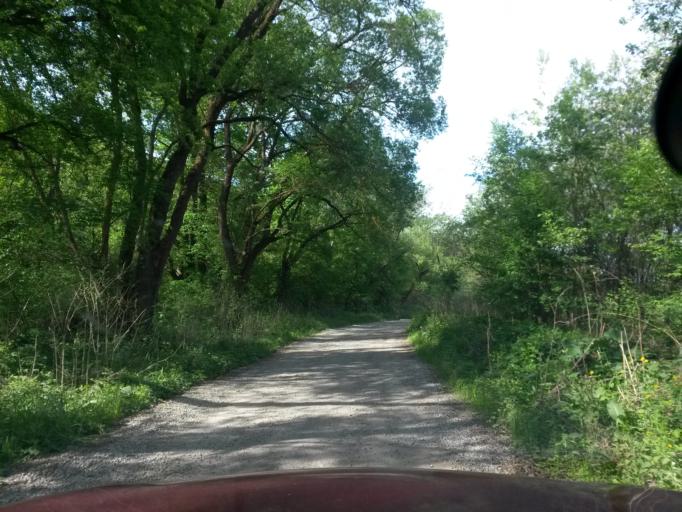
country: SK
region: Kosicky
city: Kosice
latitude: 48.7784
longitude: 21.2409
